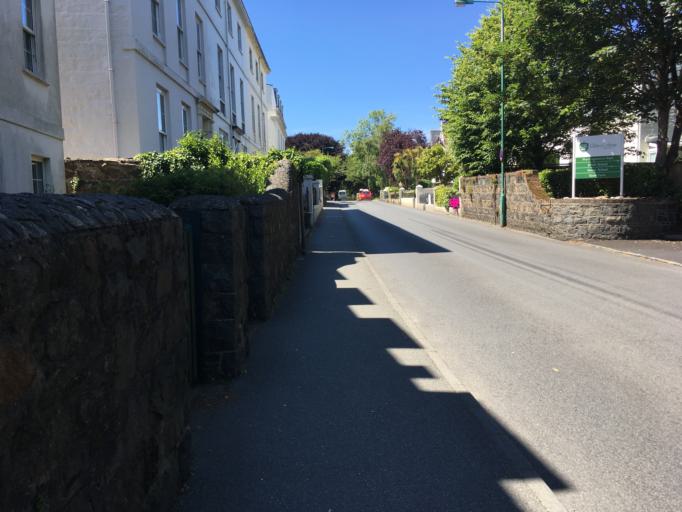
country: GG
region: St Peter Port
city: Saint Peter Port
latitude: 49.4562
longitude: -2.5502
